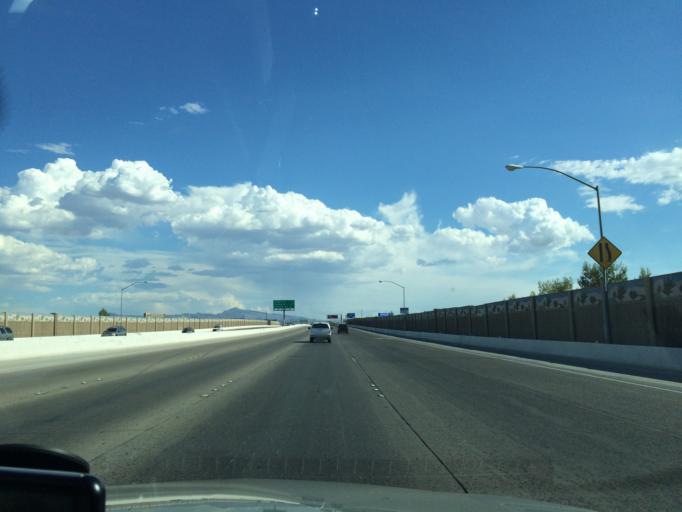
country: US
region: Nevada
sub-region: Clark County
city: Winchester
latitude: 36.1499
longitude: -115.0916
